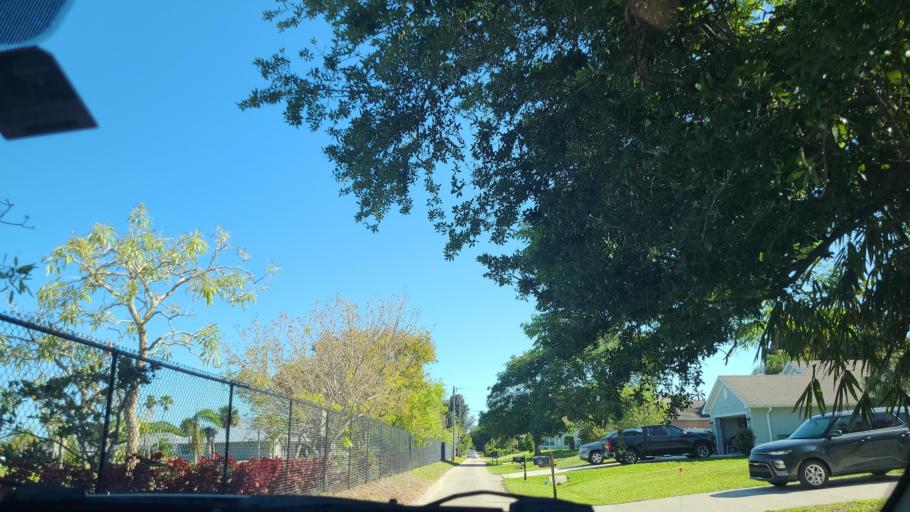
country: US
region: Florida
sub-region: Indian River County
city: Sebastian
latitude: 27.7580
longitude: -80.4784
